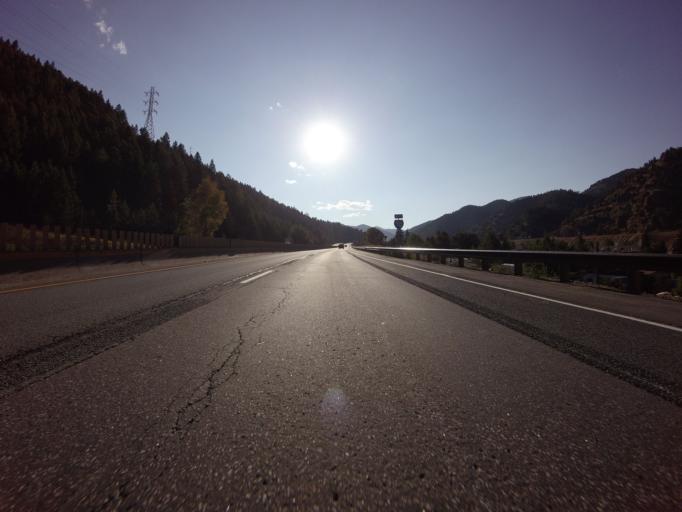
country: US
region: Colorado
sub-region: Clear Creek County
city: Idaho Springs
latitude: 39.7403
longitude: -105.5012
